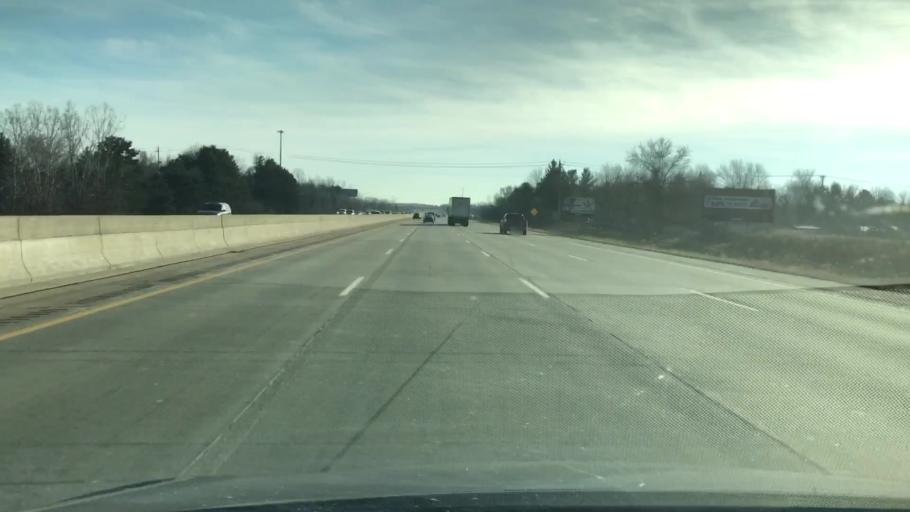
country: US
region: Michigan
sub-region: Genesee County
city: Clio
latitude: 43.1865
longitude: -83.7691
